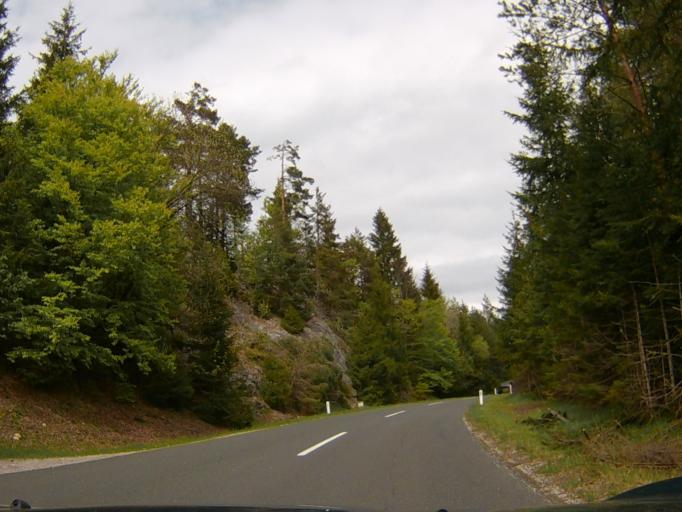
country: AT
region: Carinthia
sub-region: Villach Stadt
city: Villach
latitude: 46.5883
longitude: 13.8015
